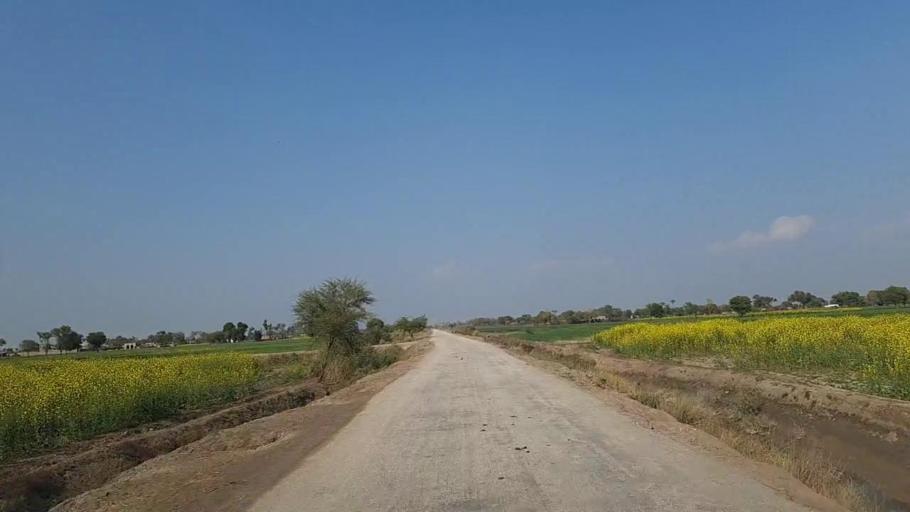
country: PK
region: Sindh
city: Jam Sahib
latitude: 26.2912
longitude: 68.5831
